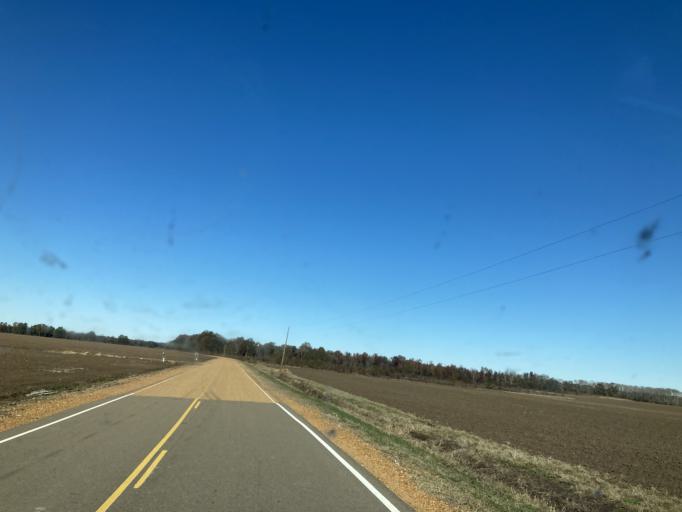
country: US
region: Mississippi
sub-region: Yazoo County
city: Yazoo City
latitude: 32.7415
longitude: -90.6345
